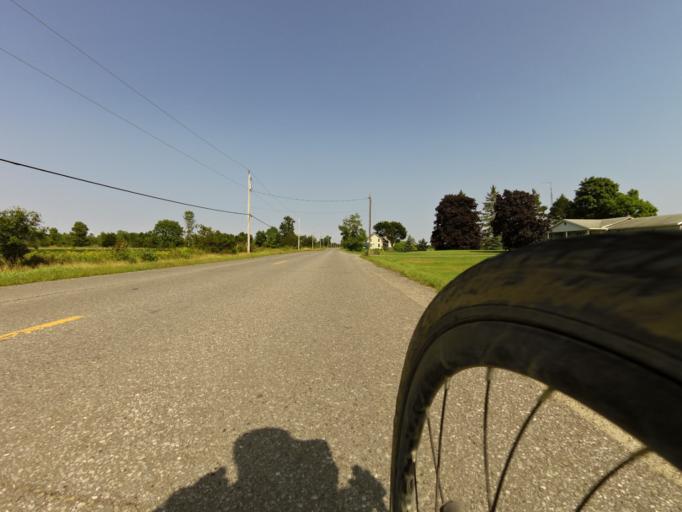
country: CA
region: Ontario
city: Skatepark
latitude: 44.2461
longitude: -76.7284
